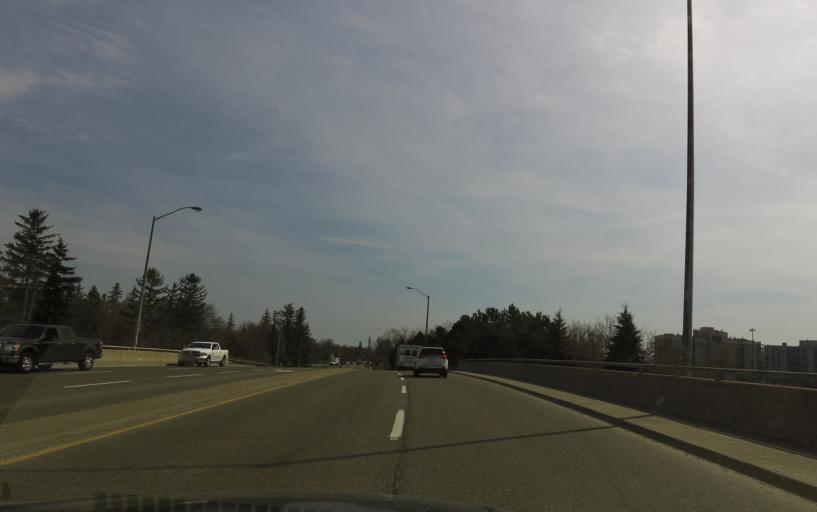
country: CA
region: Ontario
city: Oshawa
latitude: 43.8644
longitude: -78.9358
